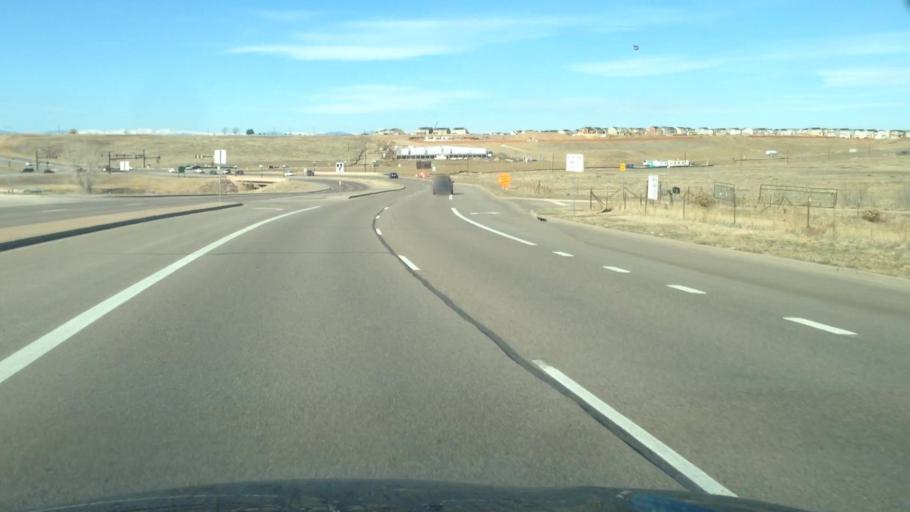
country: US
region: Colorado
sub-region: Douglas County
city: Stonegate
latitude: 39.5153
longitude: -104.8083
